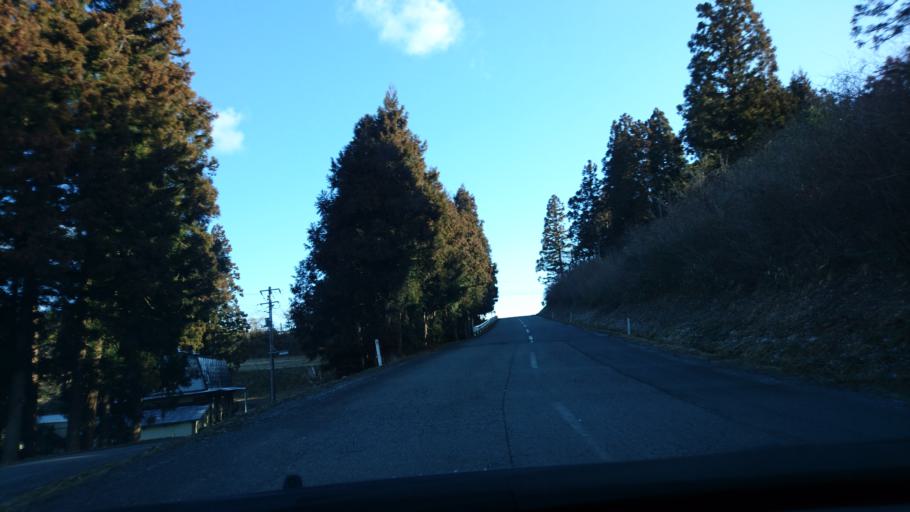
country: JP
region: Iwate
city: Ichinoseki
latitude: 38.8737
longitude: 141.2941
